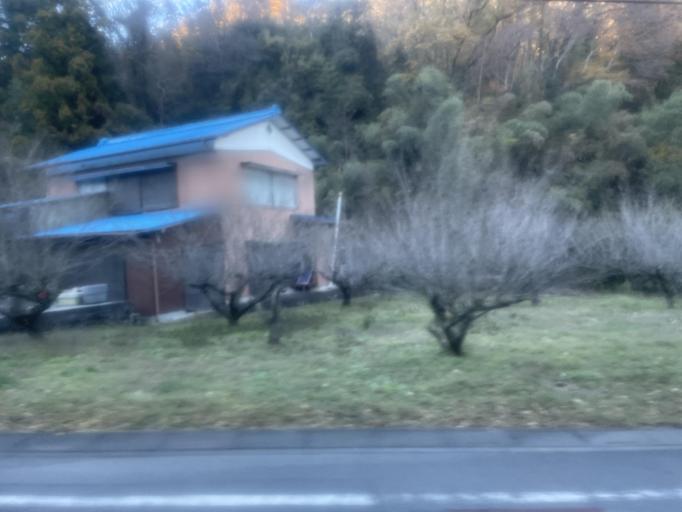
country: JP
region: Saitama
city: Yorii
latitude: 36.0824
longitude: 139.1743
